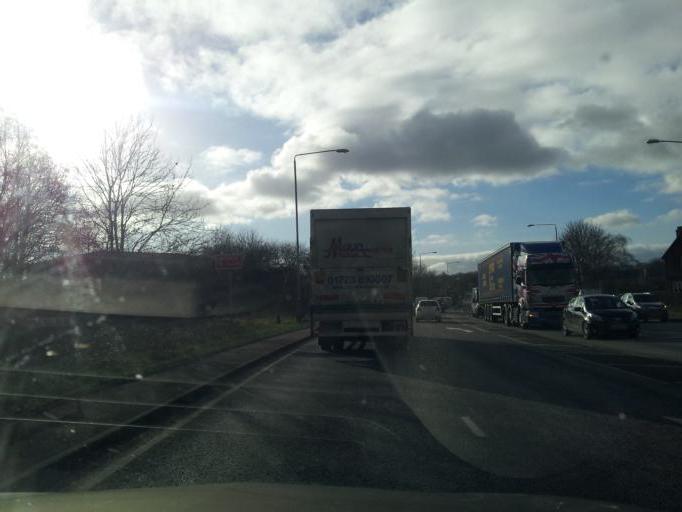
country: GB
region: England
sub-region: Nottinghamshire
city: Sutton in Ashfield
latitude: 53.1259
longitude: -1.2386
